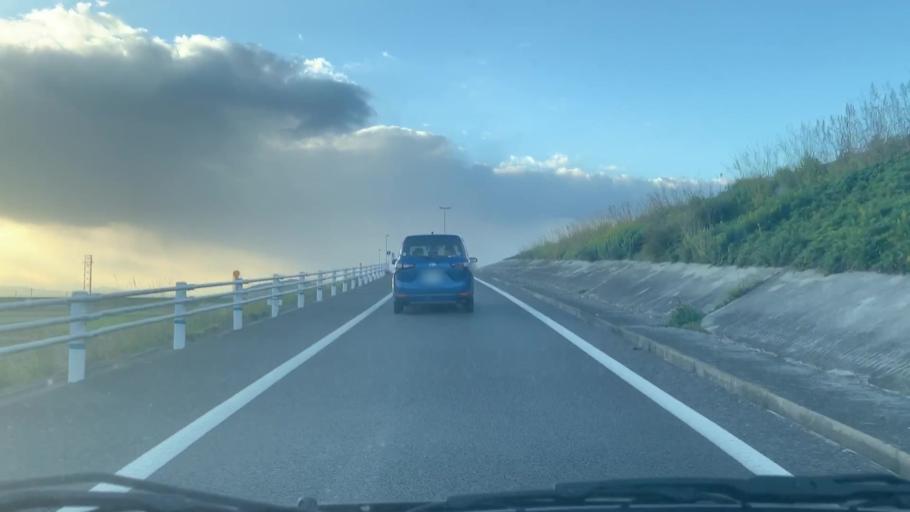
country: JP
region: Saga Prefecture
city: Saga-shi
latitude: 33.2316
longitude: 130.2567
